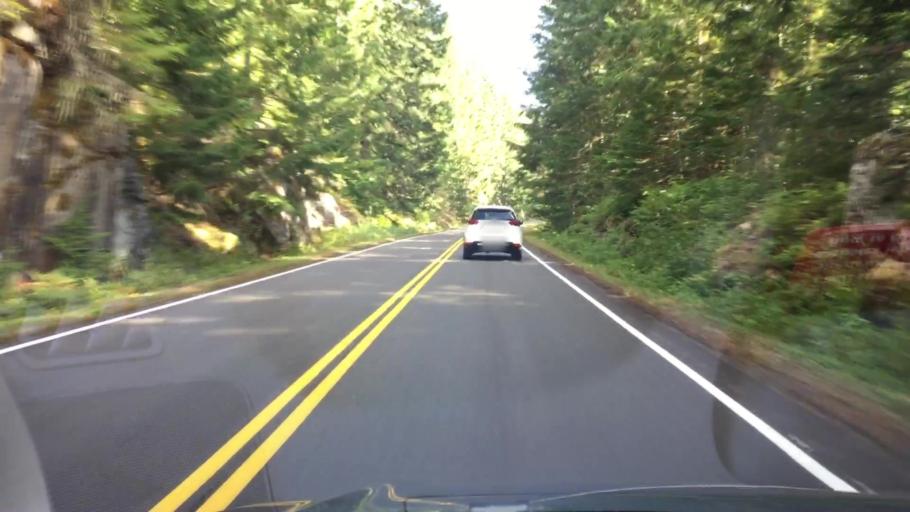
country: US
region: Washington
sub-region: Pierce County
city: Buckley
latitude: 46.7311
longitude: -121.6109
